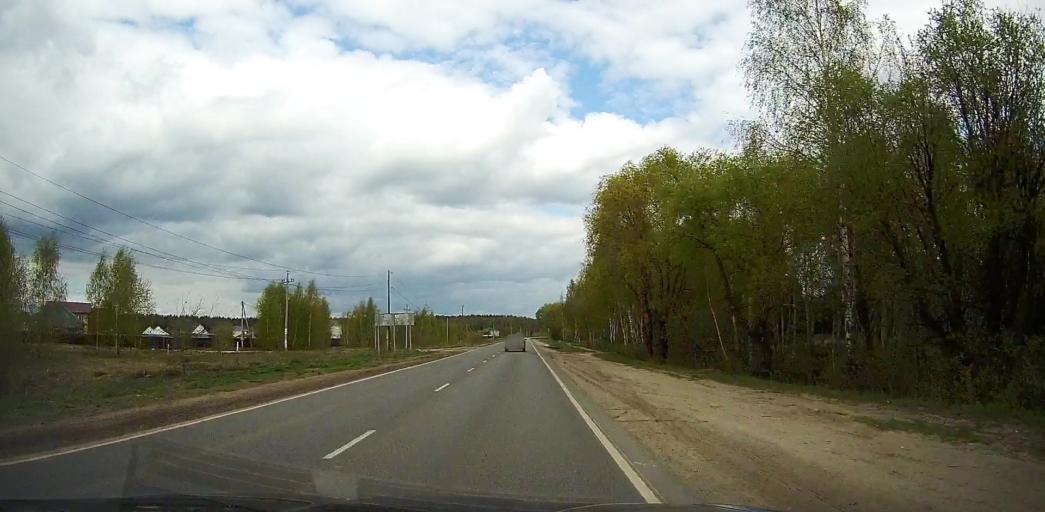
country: RU
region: Moskovskaya
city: Ashitkovo
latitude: 55.4283
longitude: 38.5783
